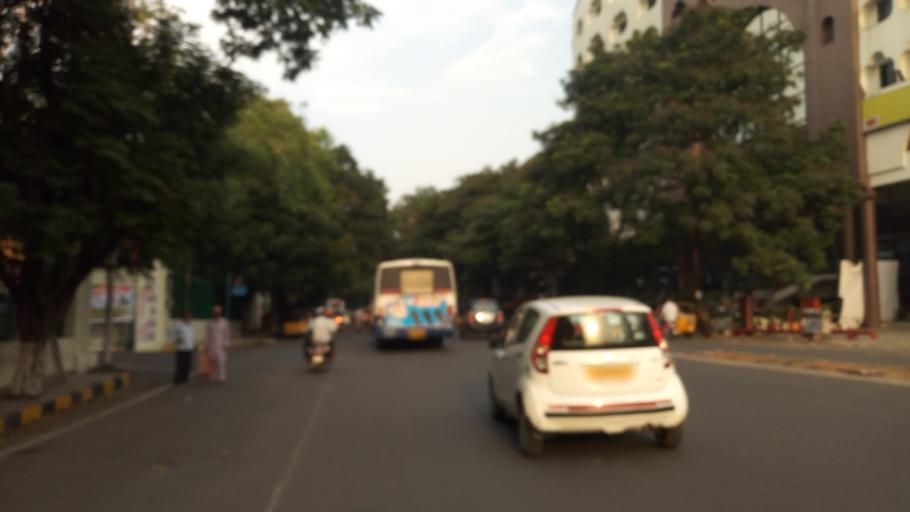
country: IN
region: Telangana
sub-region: Hyderabad
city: Hyderabad
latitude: 17.3987
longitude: 78.4719
